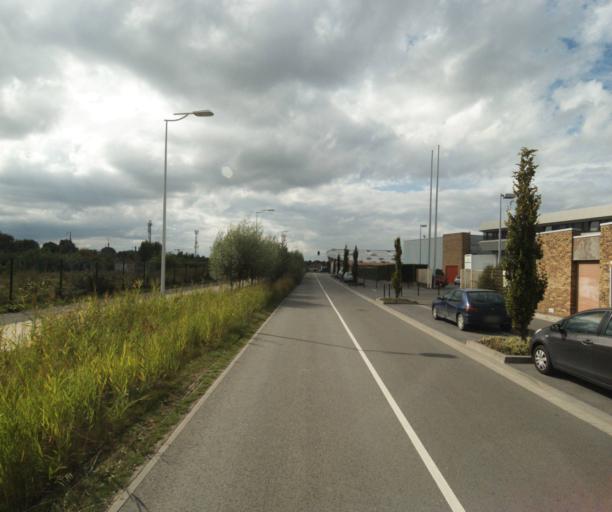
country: FR
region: Nord-Pas-de-Calais
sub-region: Departement du Nord
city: Marquette-lez-Lille
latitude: 50.6620
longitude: 3.0675
